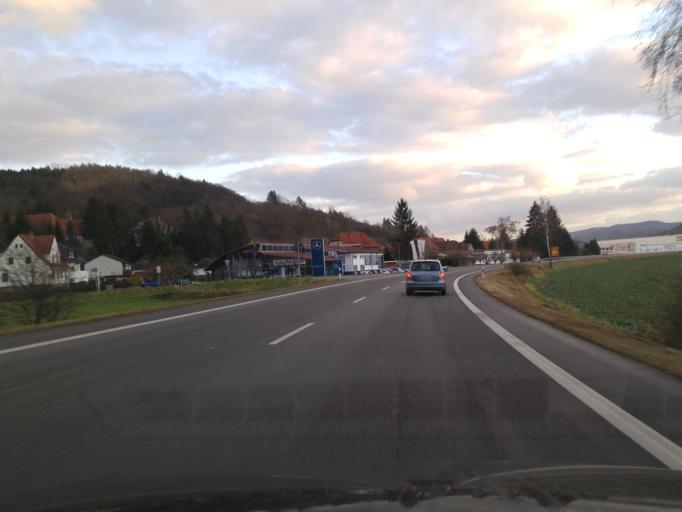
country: DE
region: Hesse
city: Witzenhausen
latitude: 51.3556
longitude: 9.8451
